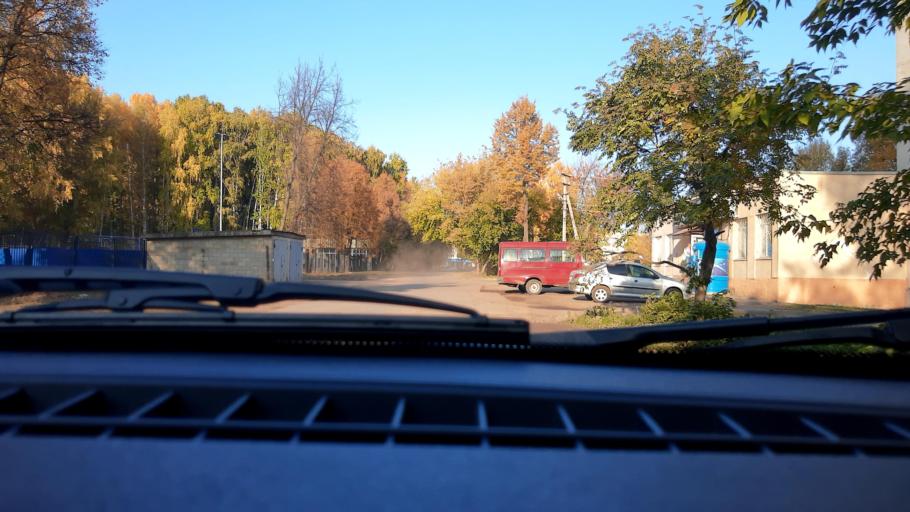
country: RU
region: Bashkortostan
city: Mikhaylovka
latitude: 54.7880
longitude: 55.8775
